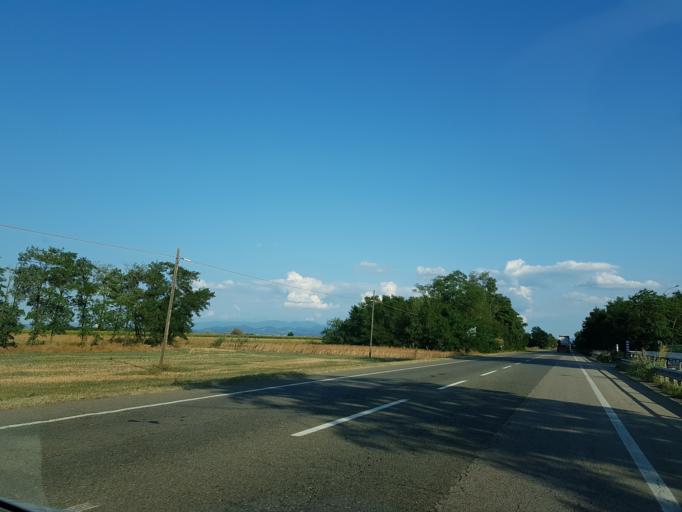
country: IT
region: Piedmont
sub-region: Provincia di Alessandria
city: Litta Parodi-Cascinagrossa
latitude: 44.8493
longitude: 8.7210
